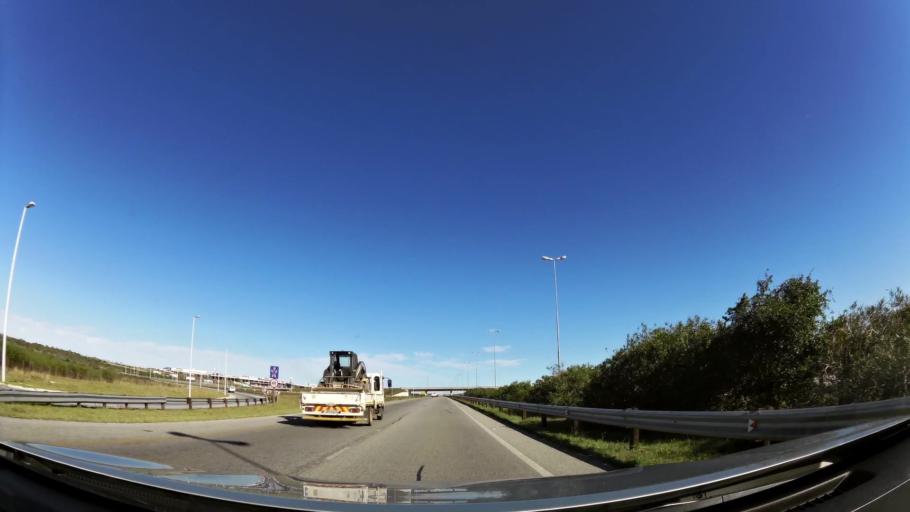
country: ZA
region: Eastern Cape
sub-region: Nelson Mandela Bay Metropolitan Municipality
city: Port Elizabeth
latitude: -33.9467
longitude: 25.4692
